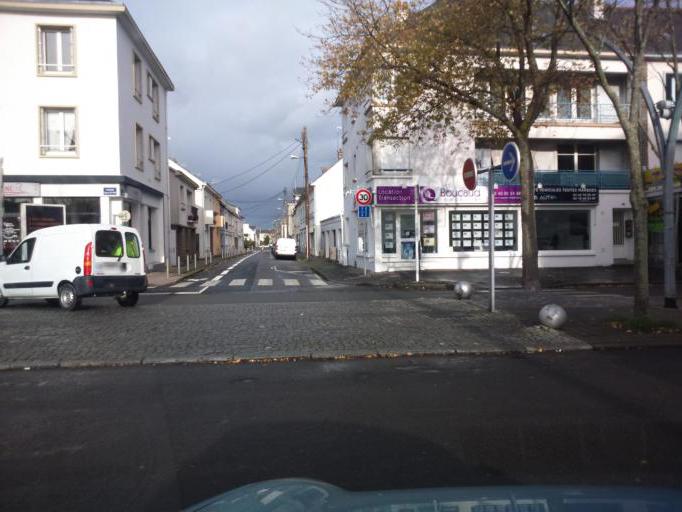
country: FR
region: Pays de la Loire
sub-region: Departement de la Loire-Atlantique
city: Saint-Nazaire
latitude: 47.2784
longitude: -2.2107
